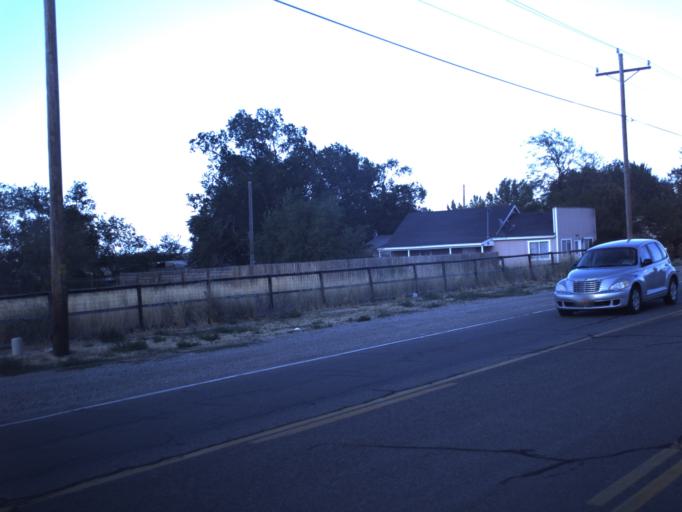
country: US
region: Utah
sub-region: Tooele County
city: Grantsville
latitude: 40.5996
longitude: -112.4334
